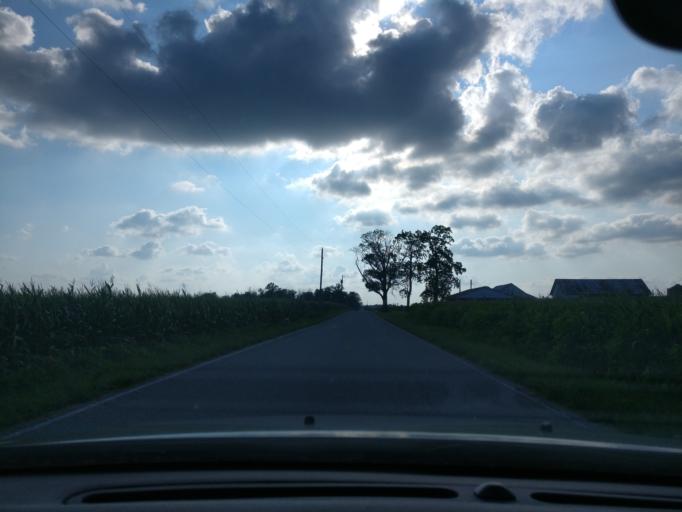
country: US
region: Ohio
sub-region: Clinton County
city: Wilmington
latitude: 39.5360
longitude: -83.8139
